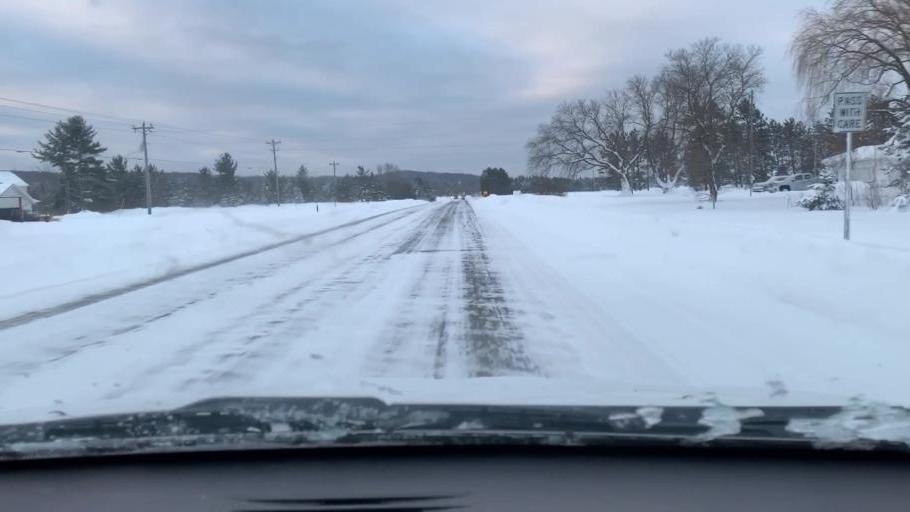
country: US
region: Michigan
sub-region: Antrim County
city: Mancelona
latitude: 44.9182
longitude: -85.0510
